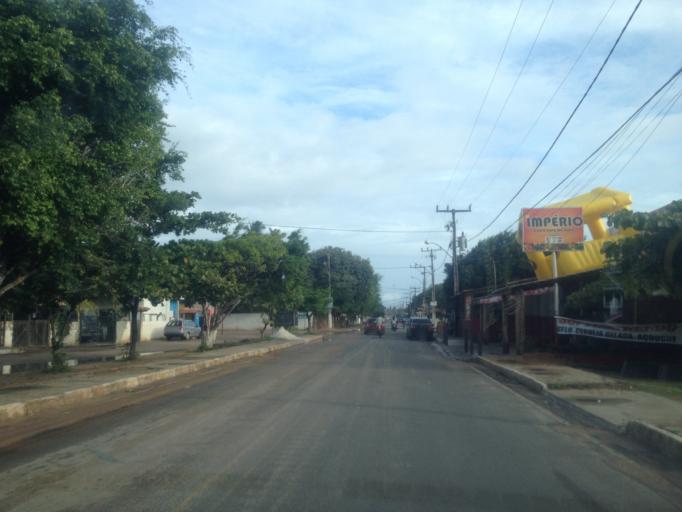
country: BR
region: Bahia
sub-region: Mata De Sao Joao
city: Mata de Sao Joao
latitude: -12.3840
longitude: -37.8817
